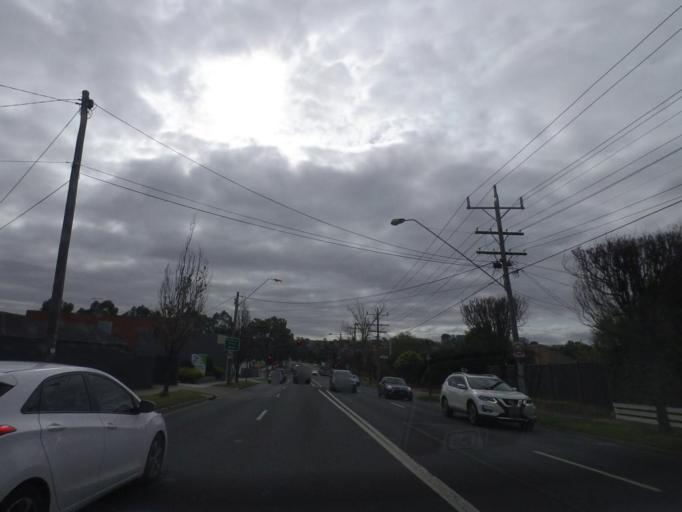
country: AU
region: Victoria
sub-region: Whitehorse
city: Box Hill North
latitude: -37.8007
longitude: 145.1180
